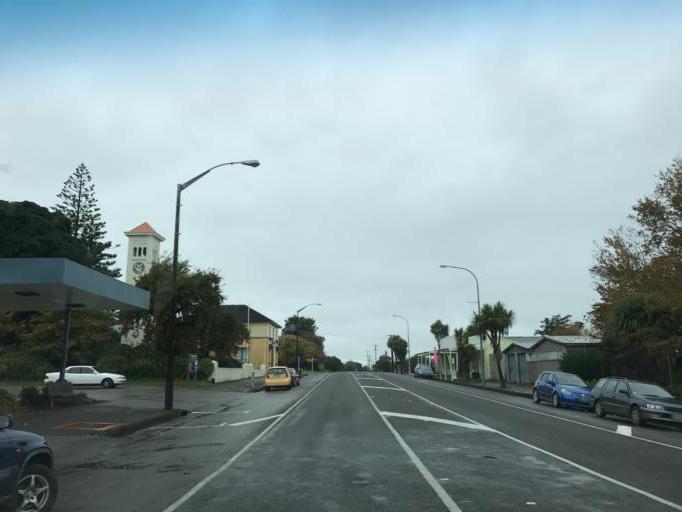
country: NZ
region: Taranaki
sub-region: South Taranaki District
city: Patea
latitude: -39.7639
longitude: 174.6343
